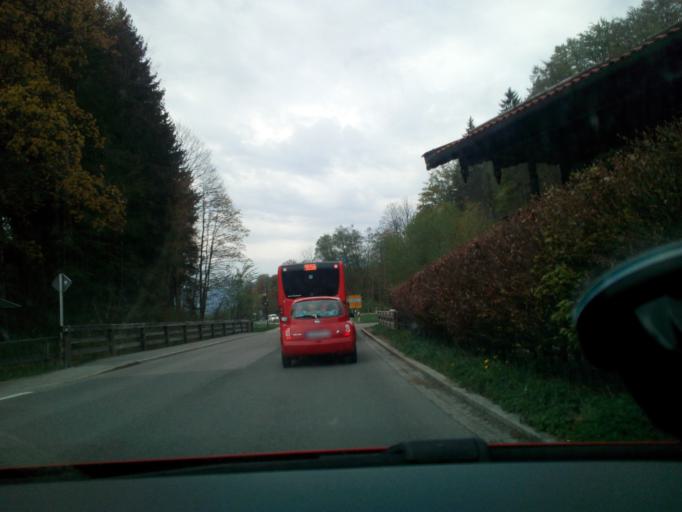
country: DE
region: Bavaria
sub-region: Upper Bavaria
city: Rottach-Egern
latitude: 47.6796
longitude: 11.7592
